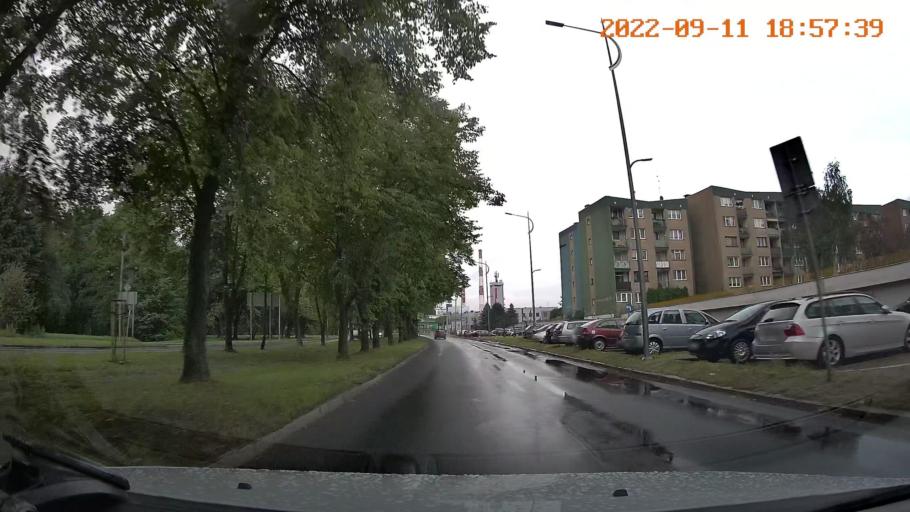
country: PL
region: Silesian Voivodeship
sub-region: Tychy
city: Cielmice
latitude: 50.1107
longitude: 19.0041
